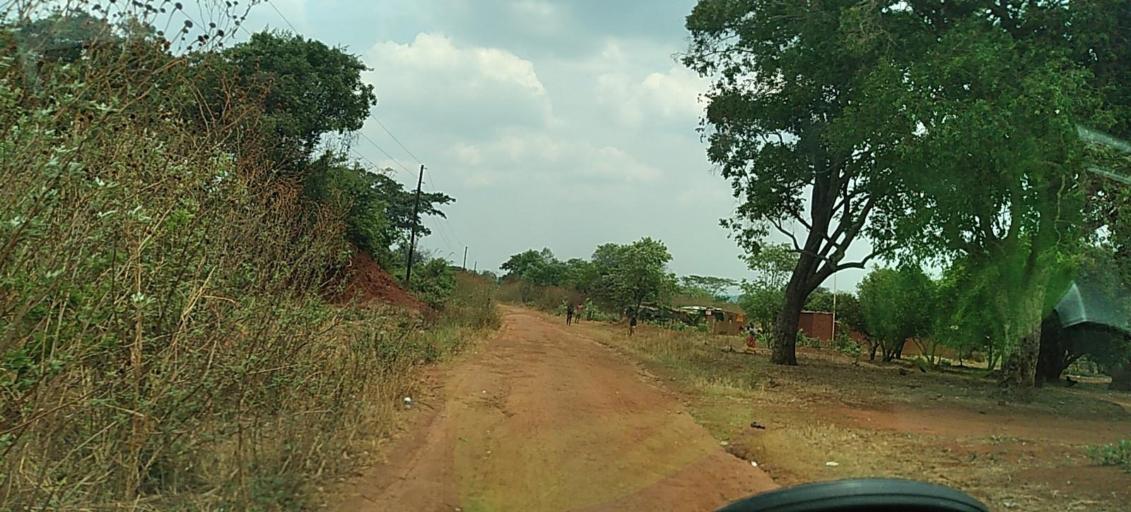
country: ZM
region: North-Western
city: Kansanshi
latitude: -12.0391
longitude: 26.3988
